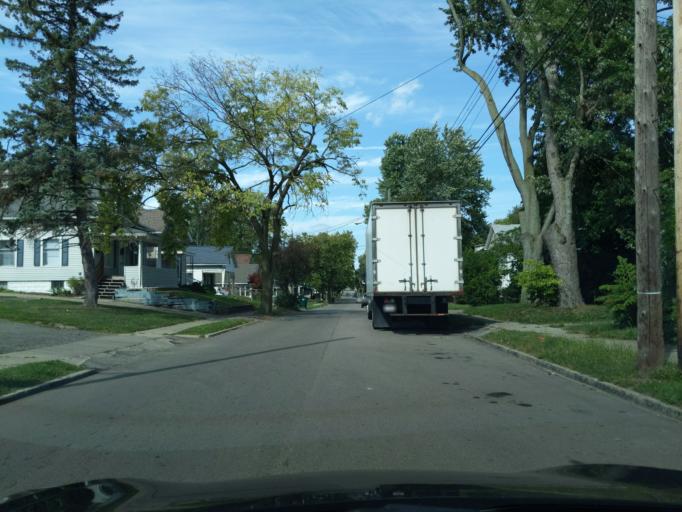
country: US
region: Michigan
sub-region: Ingham County
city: Lansing
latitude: 42.7123
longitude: -84.5419
